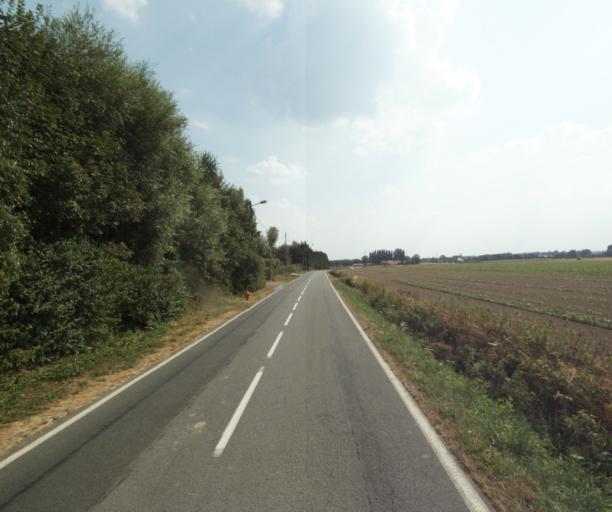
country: FR
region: Nord-Pas-de-Calais
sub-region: Departement du Nord
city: Linselles
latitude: 50.7339
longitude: 3.0638
